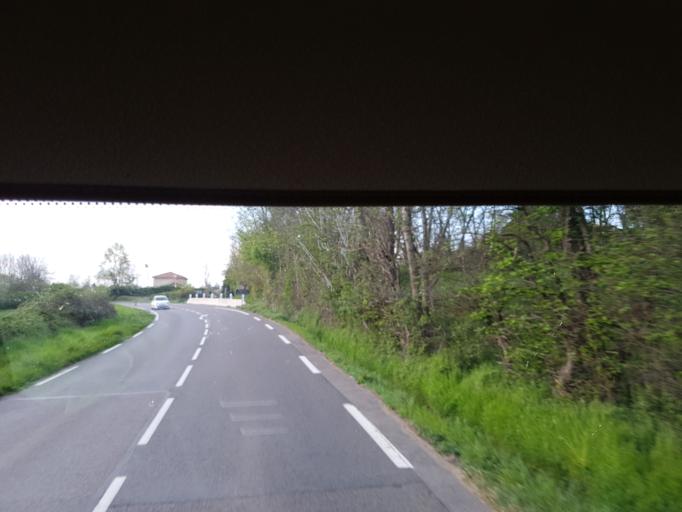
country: FR
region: Rhone-Alpes
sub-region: Departement du Rhone
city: Lentilly
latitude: 45.8049
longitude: 4.6681
